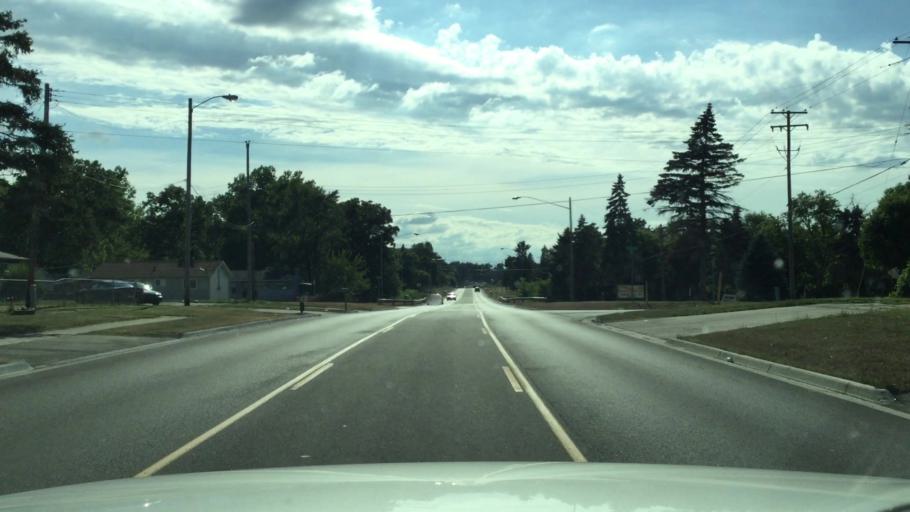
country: US
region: Michigan
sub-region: Genesee County
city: Beecher
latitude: 43.0896
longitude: -83.7244
